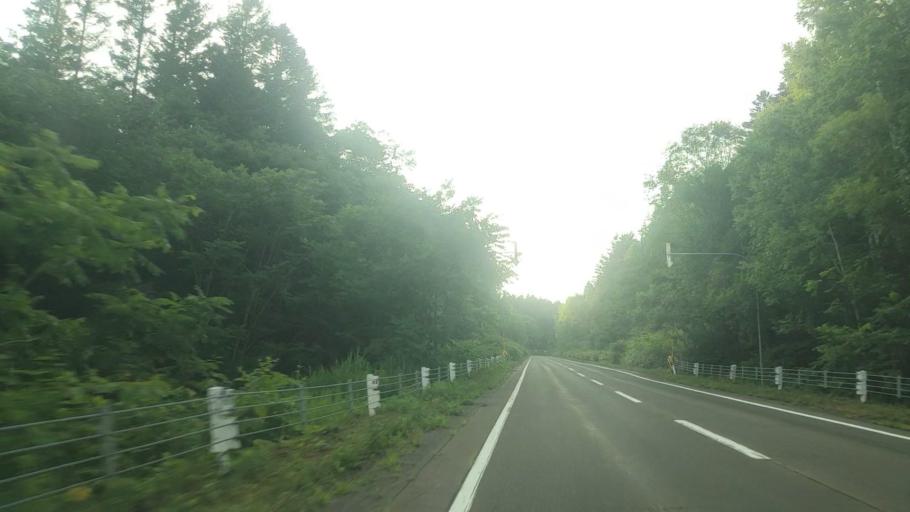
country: JP
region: Hokkaido
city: Bibai
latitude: 43.1401
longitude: 142.0953
